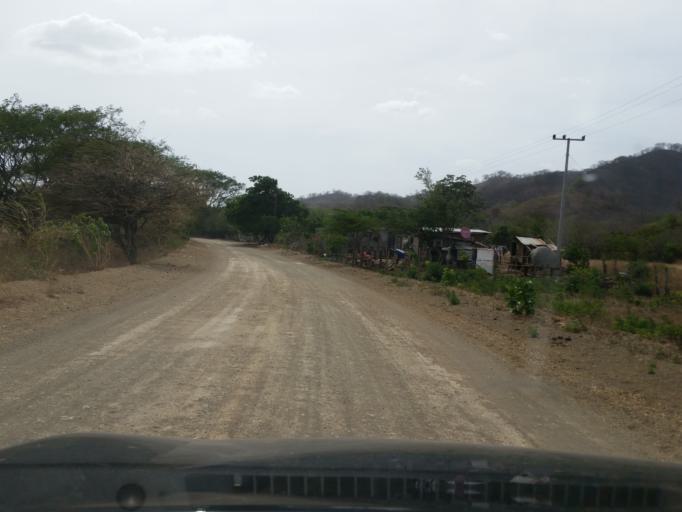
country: NI
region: Rivas
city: Tola
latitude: 11.4352
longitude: -86.0248
